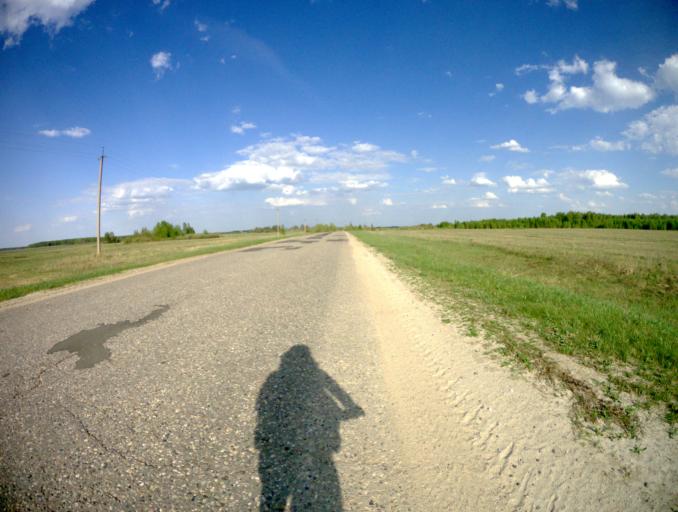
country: RU
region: Ivanovo
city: Kolobovo
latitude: 56.5402
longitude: 41.5204
